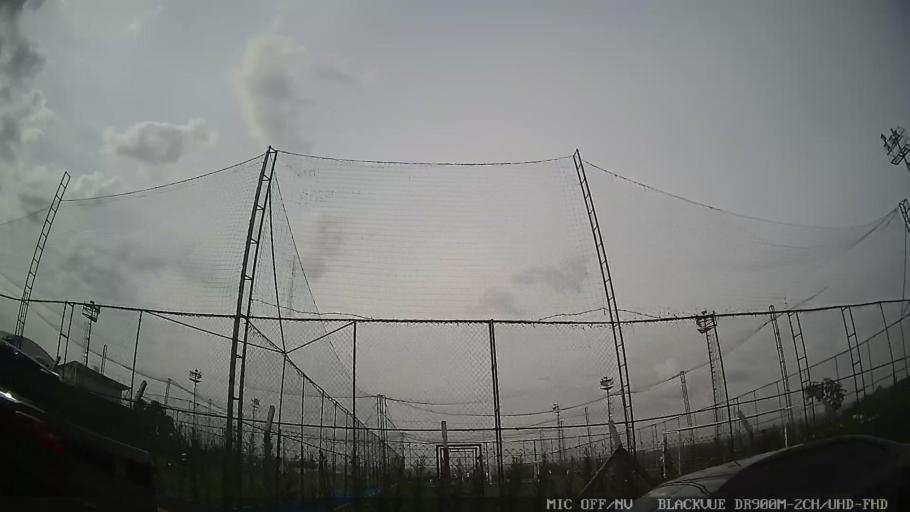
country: BR
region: Sao Paulo
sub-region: Indaiatuba
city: Indaiatuba
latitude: -23.0987
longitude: -47.1991
